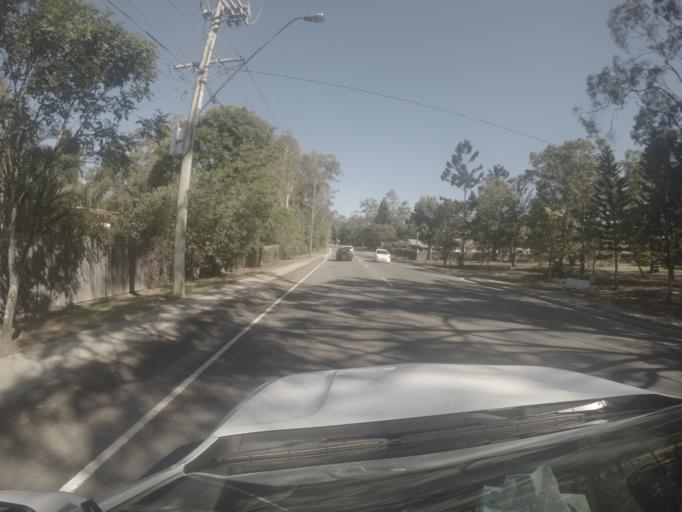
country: AU
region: Queensland
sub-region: Ipswich
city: Springfield
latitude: -27.6311
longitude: 152.9159
